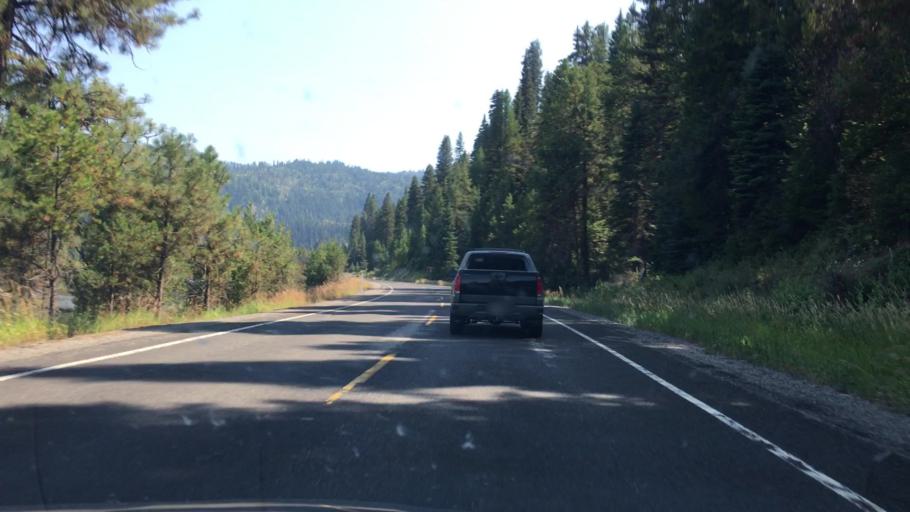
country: US
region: Idaho
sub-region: Valley County
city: Cascade
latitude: 44.2833
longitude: -116.0807
